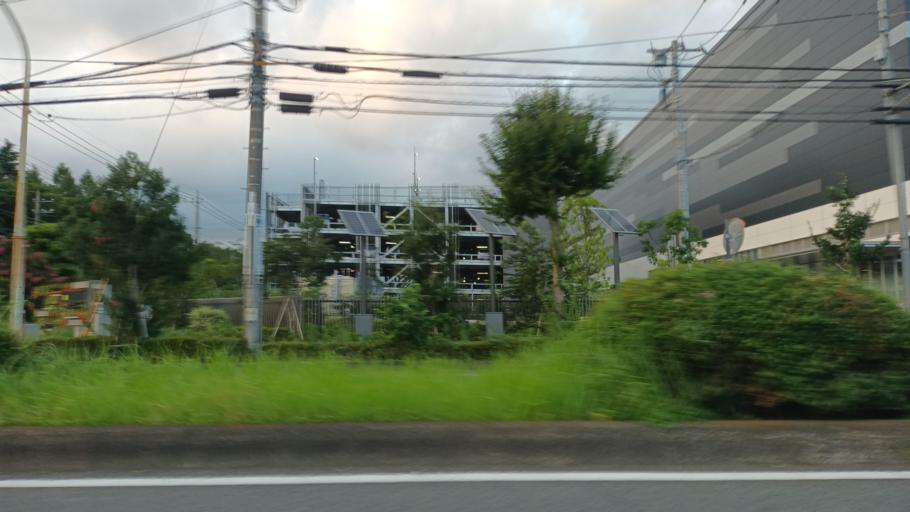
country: JP
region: Tokyo
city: Fussa
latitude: 35.7797
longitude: 139.3069
